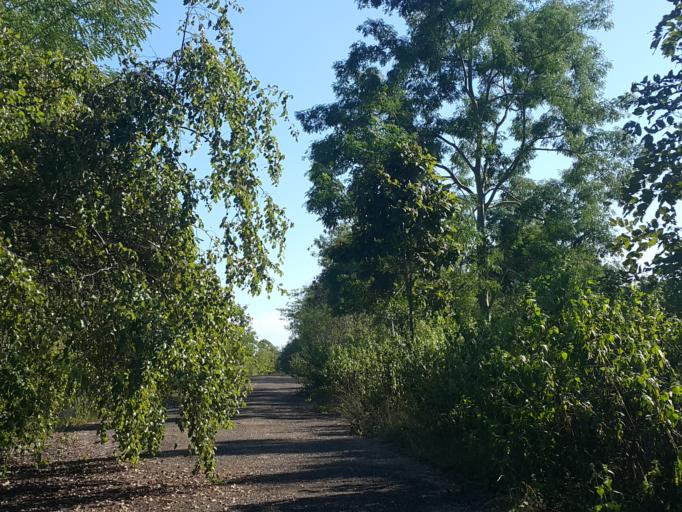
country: TH
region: Chiang Mai
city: San Sai
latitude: 18.9228
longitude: 99.1150
